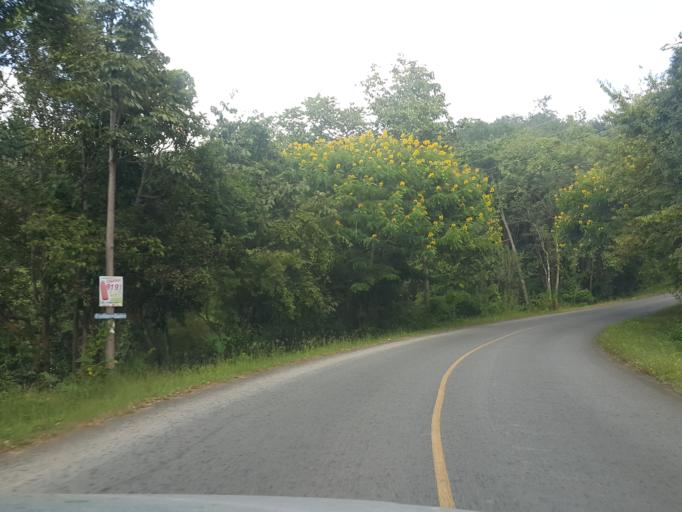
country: TH
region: Chiang Mai
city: Mae Chaem
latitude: 18.5560
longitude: 98.3913
